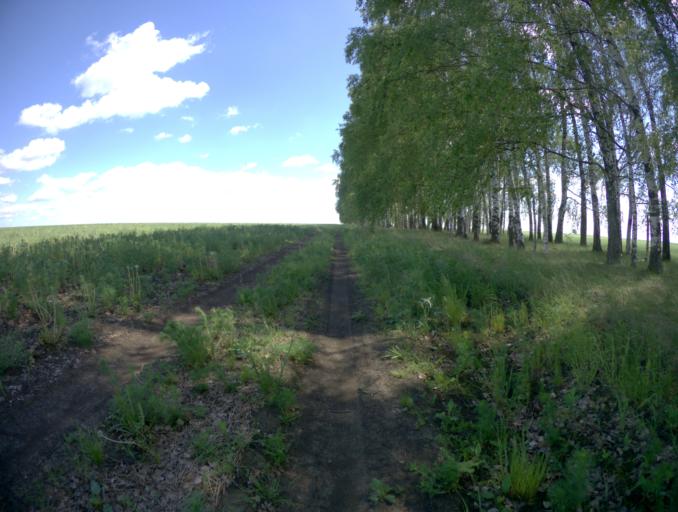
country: RU
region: Ivanovo
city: Gavrilov Posad
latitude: 56.4527
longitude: 40.2234
